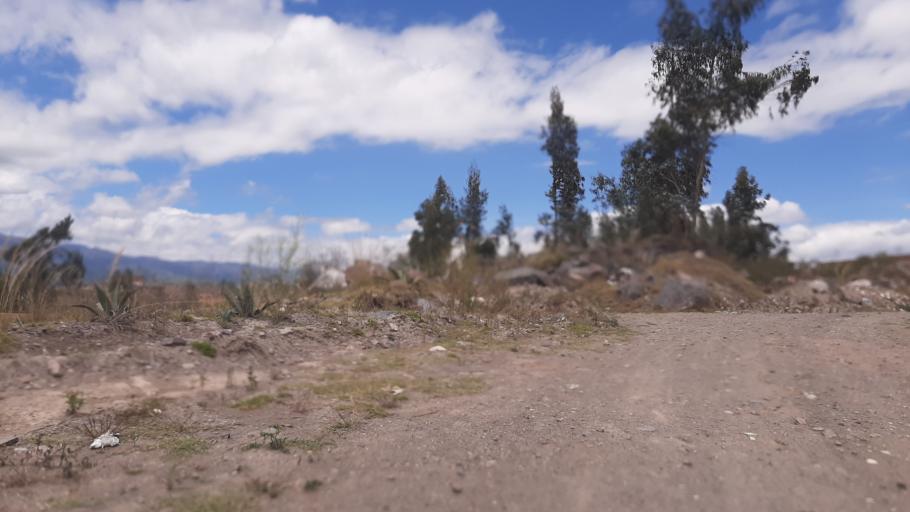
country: EC
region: Chimborazo
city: Riobamba
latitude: -1.6510
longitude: -78.6338
